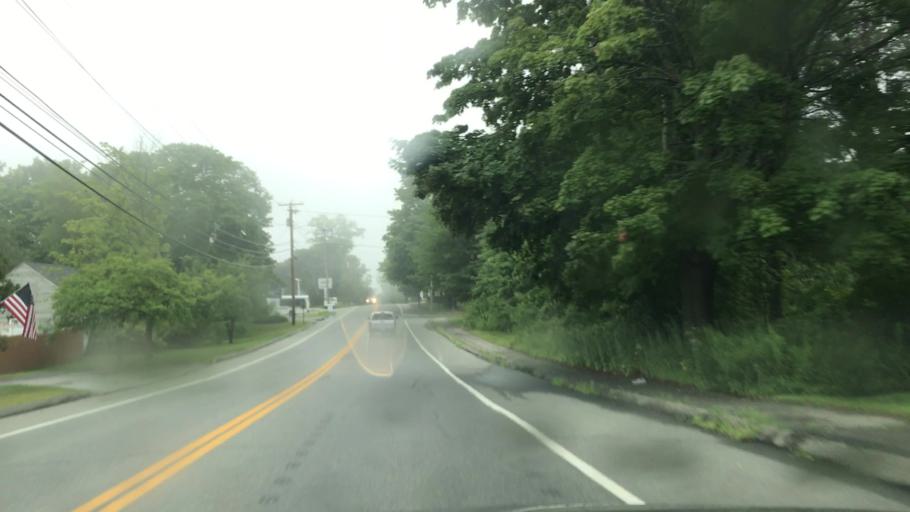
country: US
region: Maine
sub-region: Knox County
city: Camden
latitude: 44.2028
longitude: -69.0744
